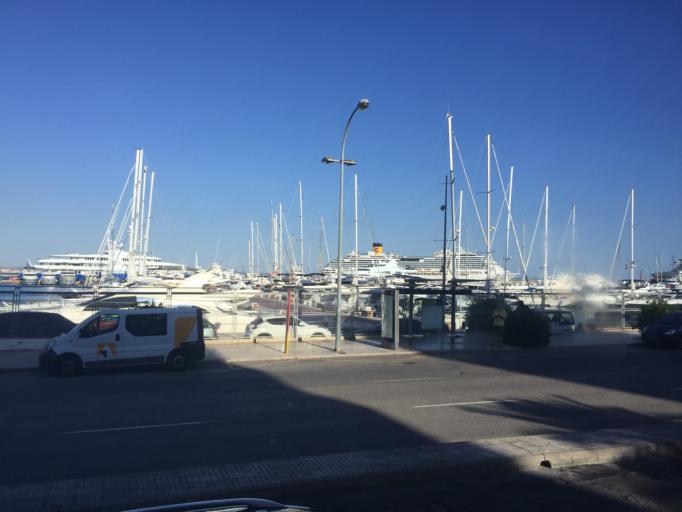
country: ES
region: Balearic Islands
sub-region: Illes Balears
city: Palma
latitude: 39.5593
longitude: 2.6266
